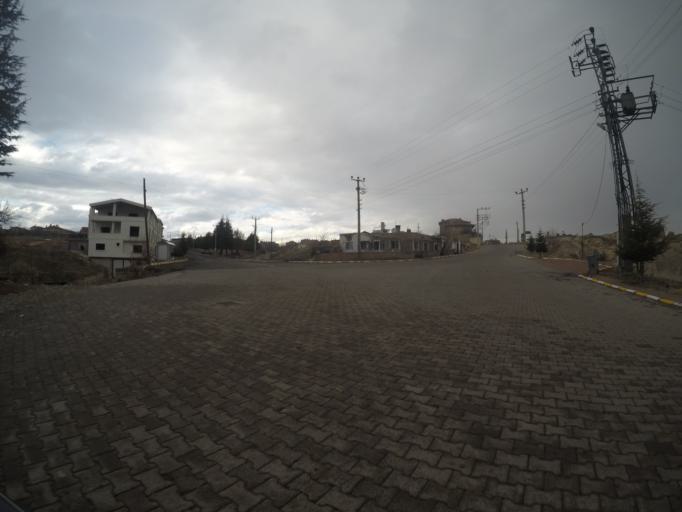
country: TR
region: Nevsehir
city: Goereme
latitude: 38.6263
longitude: 34.8600
